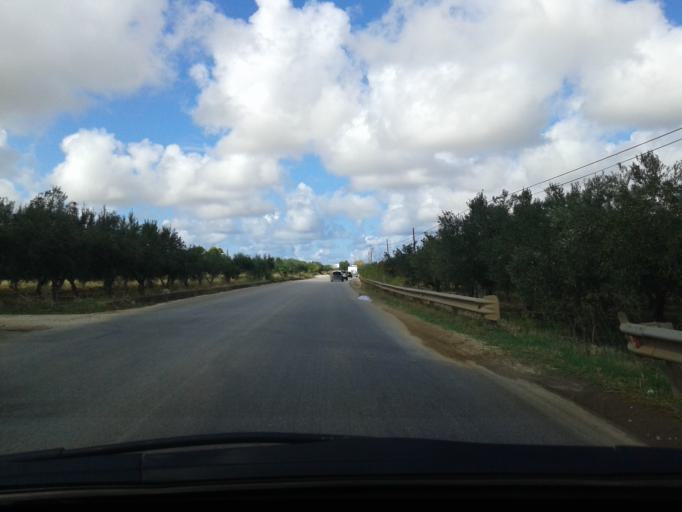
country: IT
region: Sicily
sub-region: Trapani
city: Castelluzzo
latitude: 38.0760
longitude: 12.7328
